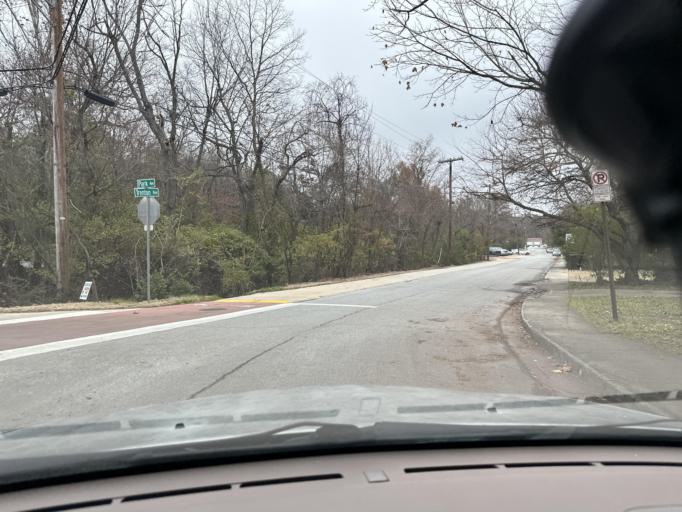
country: US
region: Arkansas
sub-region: Washington County
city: Fayetteville
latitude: 36.0726
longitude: -94.1606
